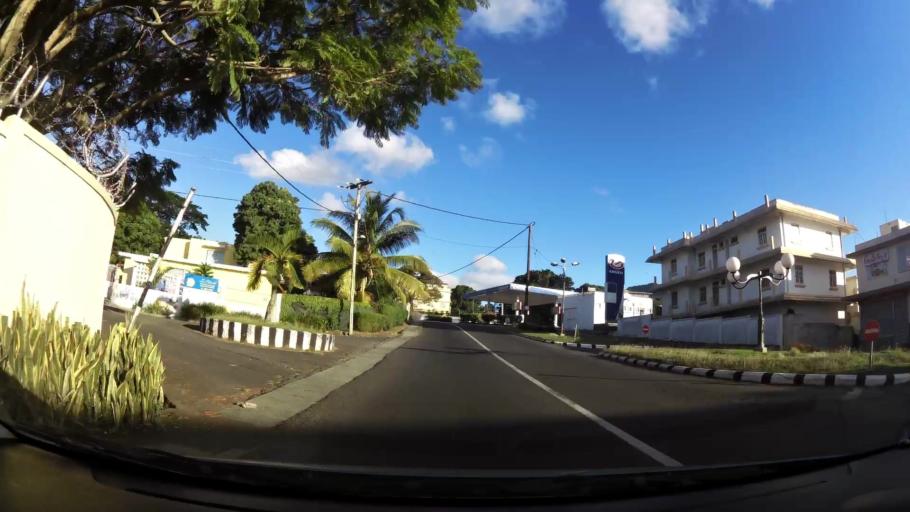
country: MU
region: Plaines Wilhems
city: Ebene
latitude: -20.2358
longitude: 57.4628
